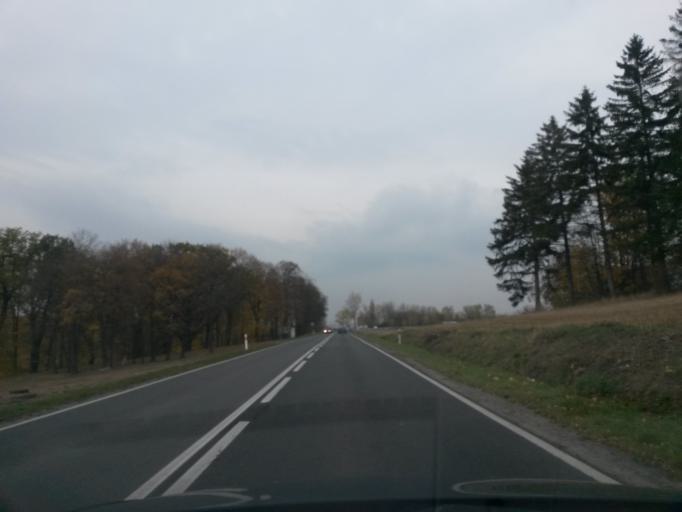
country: PL
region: Lower Silesian Voivodeship
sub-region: Powiat klodzki
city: Klodzko
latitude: 50.3871
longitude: 16.6617
